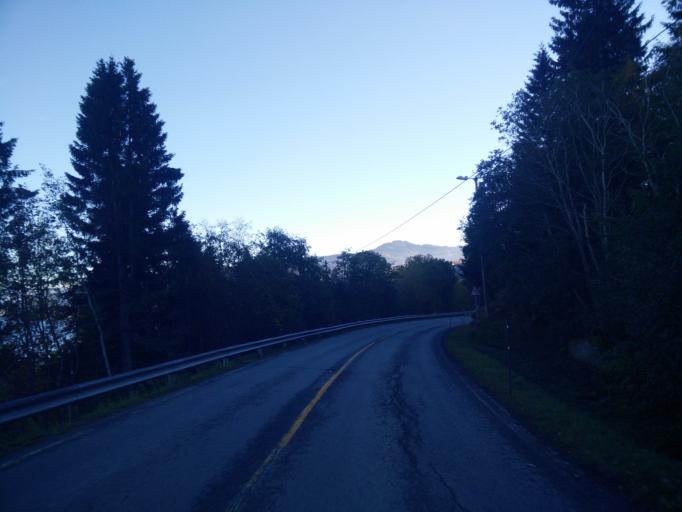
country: NO
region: Sor-Trondelag
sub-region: Skaun
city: Borsa
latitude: 63.3418
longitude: 10.0566
